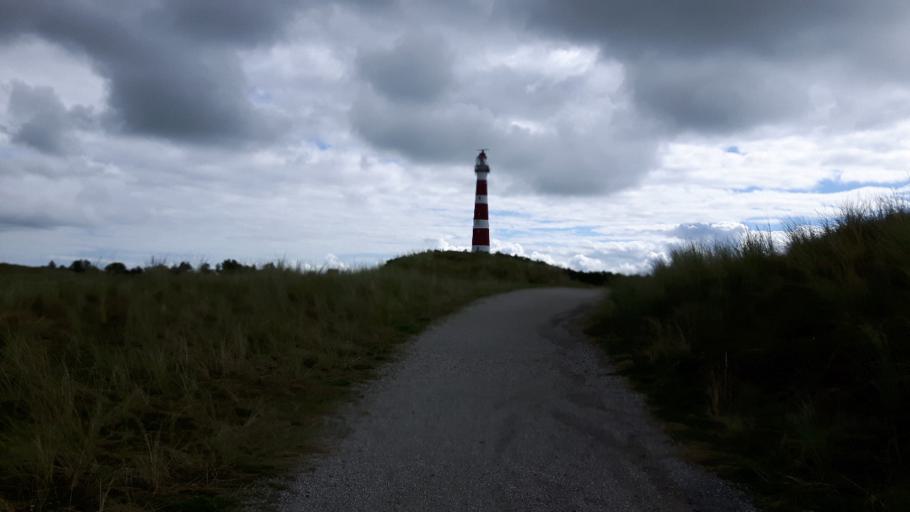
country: NL
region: Friesland
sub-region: Gemeente Ameland
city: Hollum
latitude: 53.4509
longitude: 5.6222
